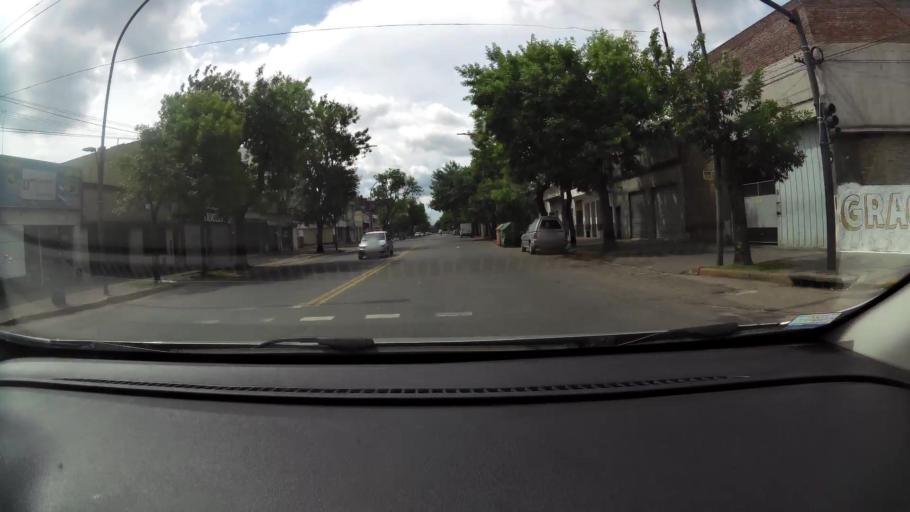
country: AR
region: Santa Fe
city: Gobernador Galvez
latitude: -33.0058
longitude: -60.6359
